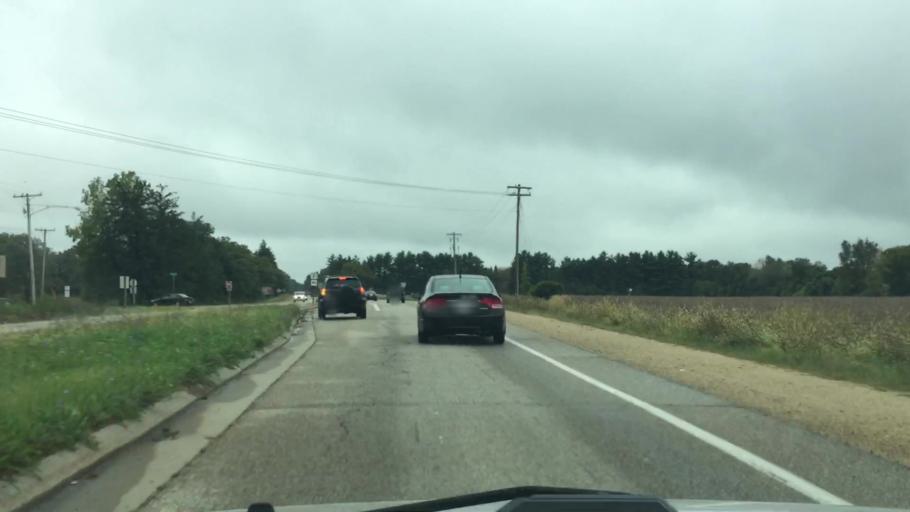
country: US
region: Wisconsin
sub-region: Rock County
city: Janesville
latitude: 42.7288
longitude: -89.0332
